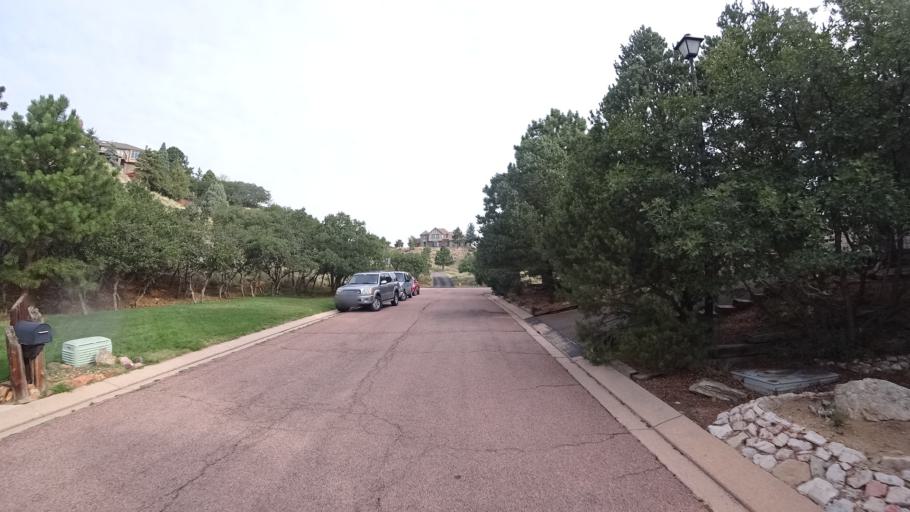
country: US
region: Colorado
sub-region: El Paso County
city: Air Force Academy
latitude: 38.9349
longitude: -104.8492
